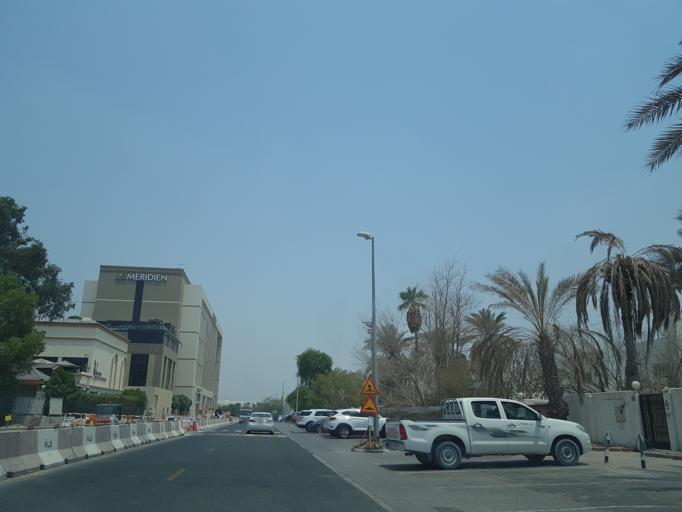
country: AE
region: Ash Shariqah
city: Sharjah
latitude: 25.2470
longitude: 55.3459
